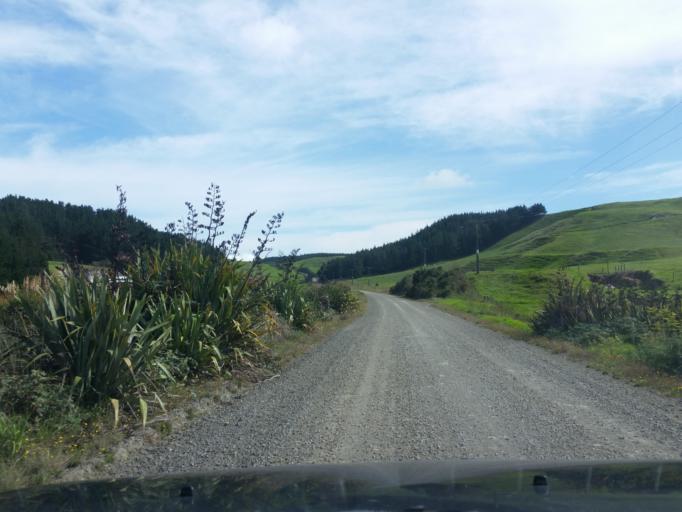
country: NZ
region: Northland
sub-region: Kaipara District
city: Dargaville
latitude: -35.9355
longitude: 173.7713
